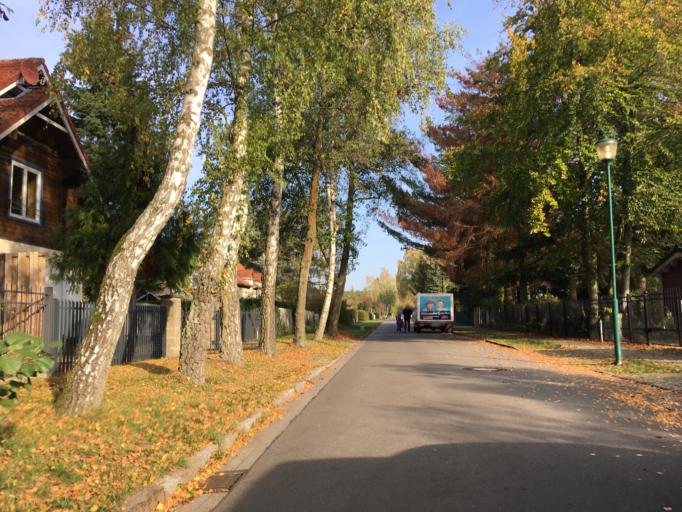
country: DE
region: Brandenburg
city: Glienicke
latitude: 52.6711
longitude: 13.3307
